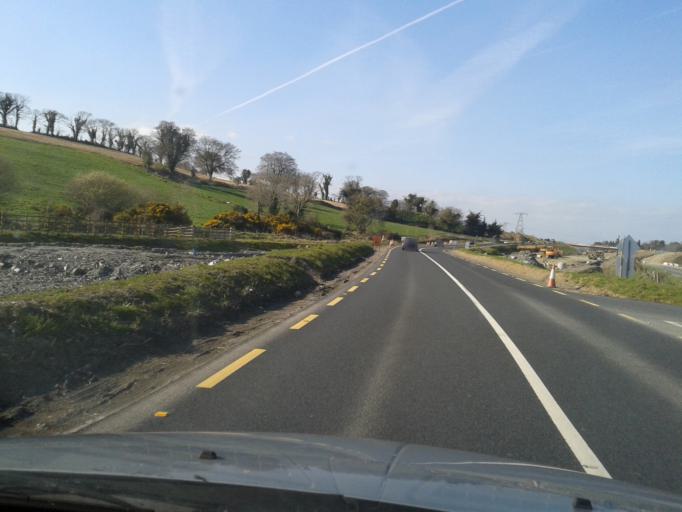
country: IE
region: Leinster
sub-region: Wicklow
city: Wicklow
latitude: 52.8974
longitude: -6.1009
